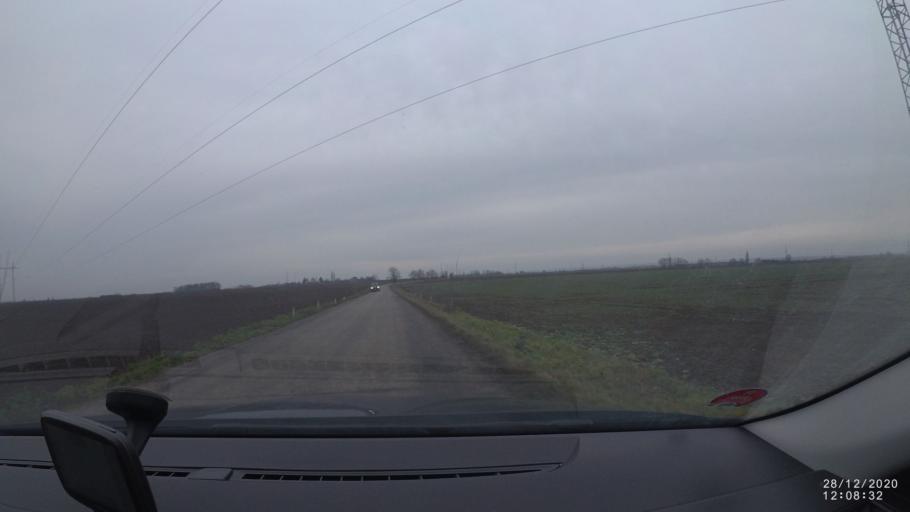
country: CZ
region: Central Bohemia
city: Zelenec
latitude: 50.1548
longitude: 14.6436
